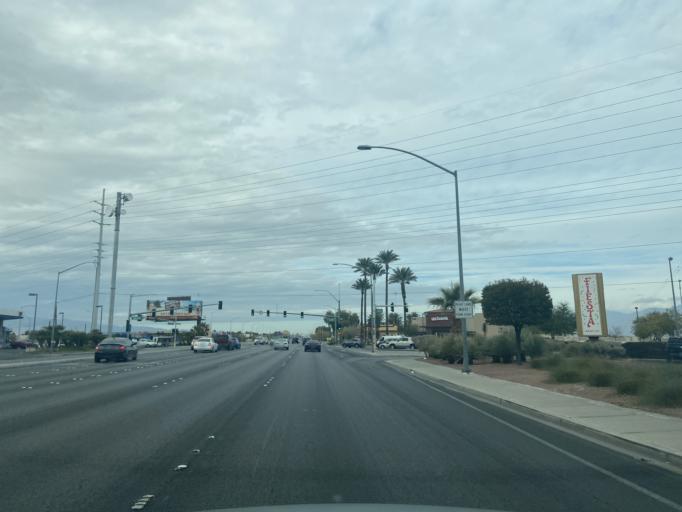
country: US
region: Nevada
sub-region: Clark County
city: Las Vegas
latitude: 36.2021
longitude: -115.1983
